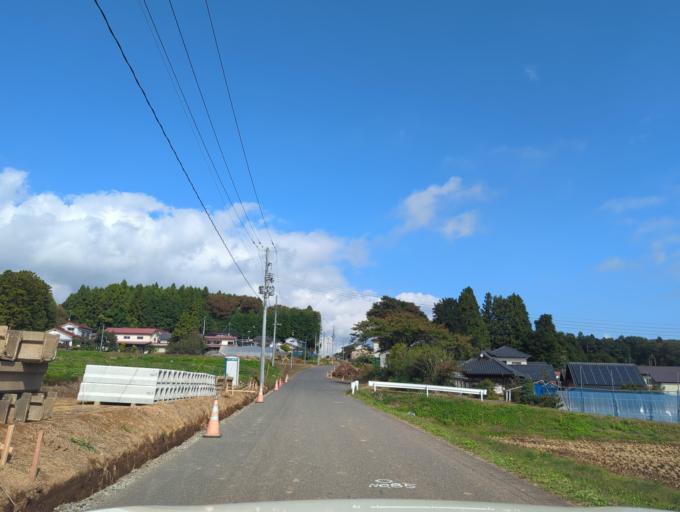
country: JP
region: Fukushima
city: Motomiya
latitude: 37.5502
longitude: 140.3437
